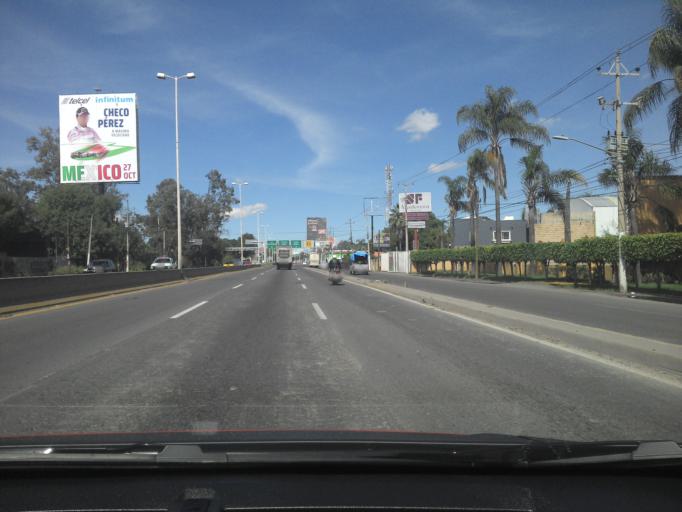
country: MX
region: Jalisco
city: Nuevo Mexico
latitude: 20.7038
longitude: -103.4619
